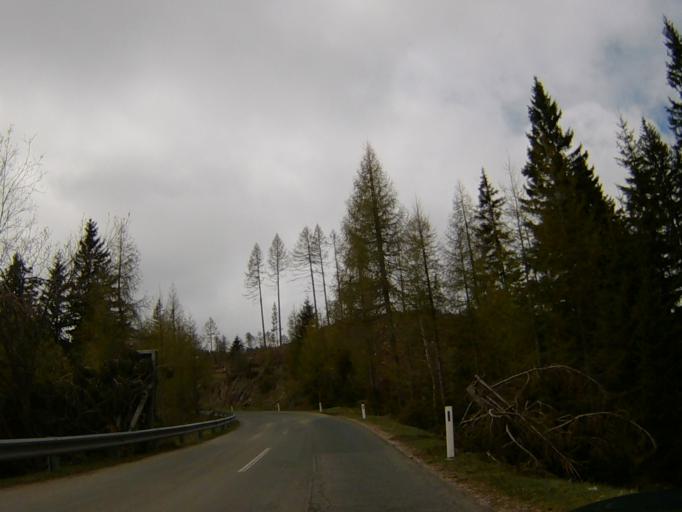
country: AT
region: Carinthia
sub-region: Politischer Bezirk Villach Land
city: Arnoldstein
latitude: 46.5926
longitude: 13.7331
